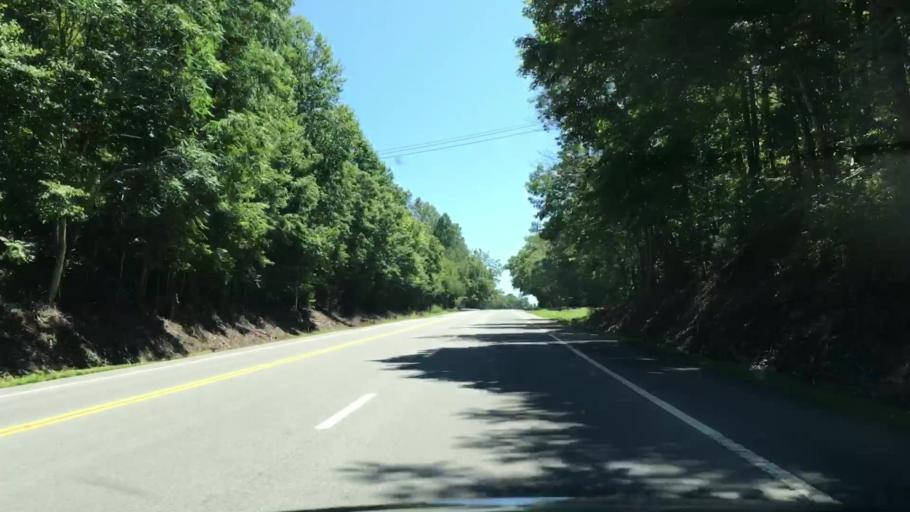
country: US
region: Tennessee
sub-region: Jackson County
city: Gainesboro
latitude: 36.3062
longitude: -85.6433
